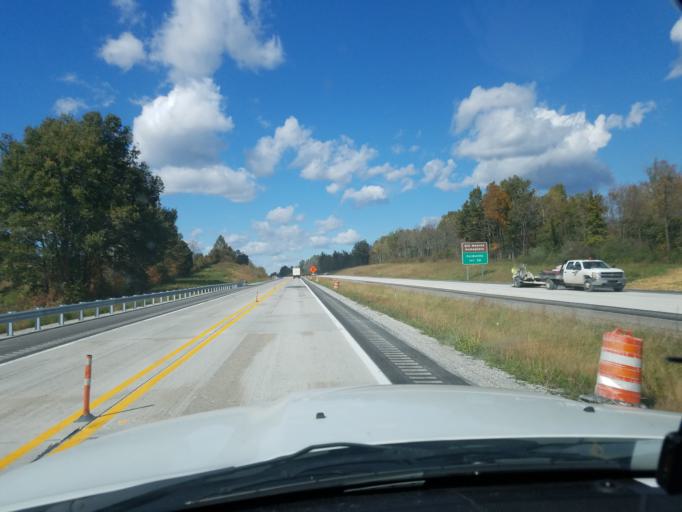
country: US
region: Kentucky
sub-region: Ohio County
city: Beaver Dam
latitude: 37.4406
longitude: -86.8582
